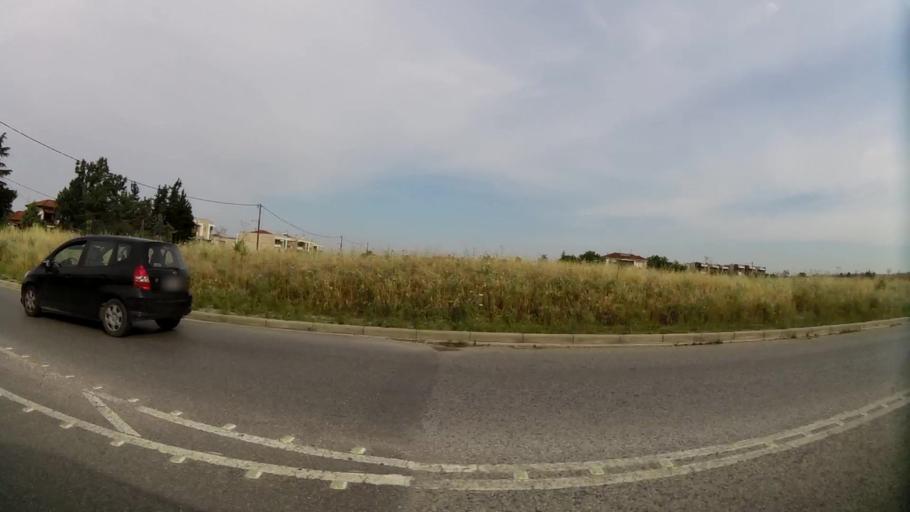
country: GR
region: Central Macedonia
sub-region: Nomos Thessalonikis
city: Thermi
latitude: 40.5493
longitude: 23.0116
